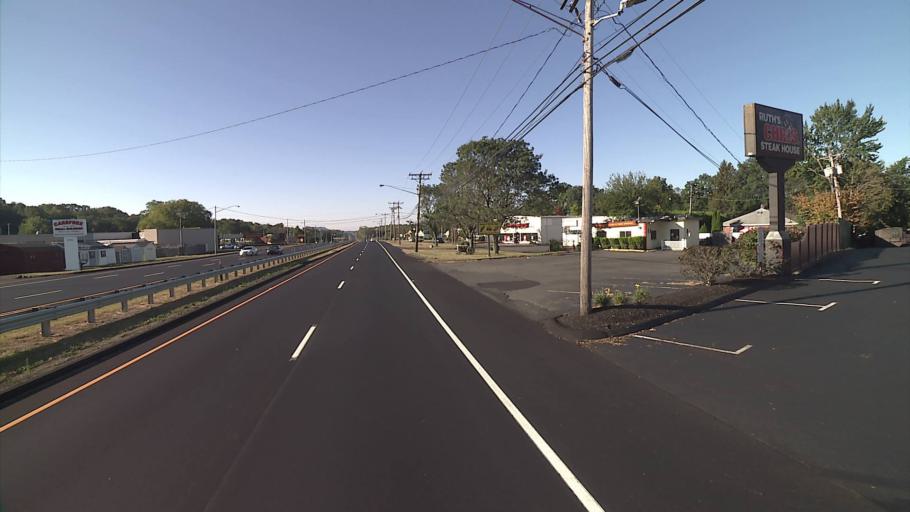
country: US
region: Connecticut
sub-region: Hartford County
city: Newington
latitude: 41.6827
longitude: -72.7106
